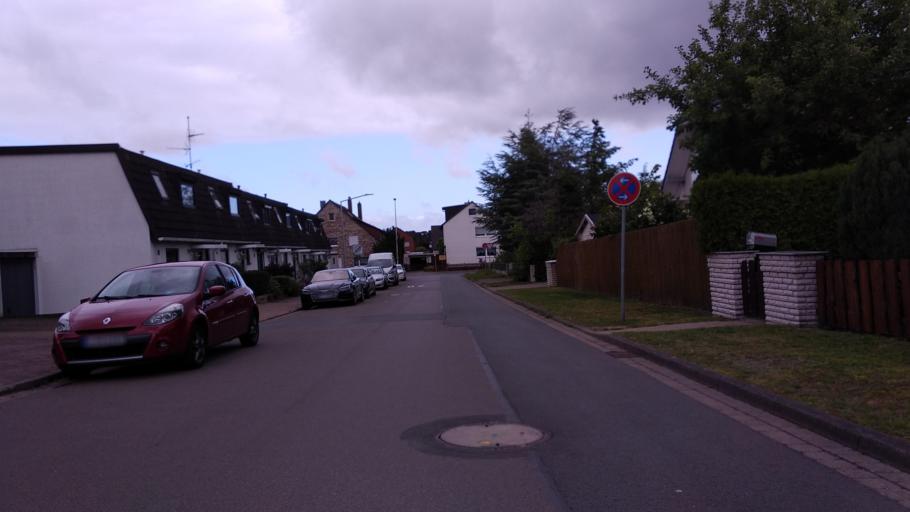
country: DE
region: Lower Saxony
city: Hagenburg
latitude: 52.4546
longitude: 9.3716
